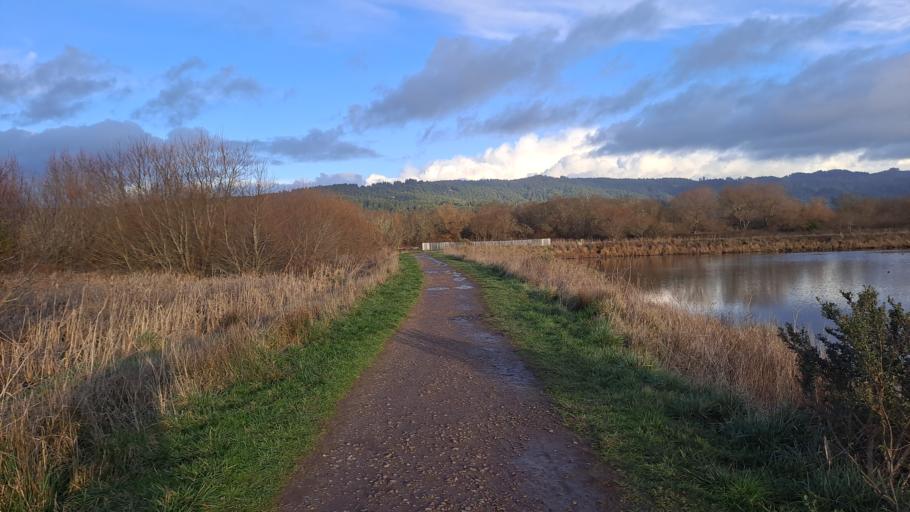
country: US
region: California
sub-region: Humboldt County
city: Arcata
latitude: 40.8633
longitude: -124.0947
